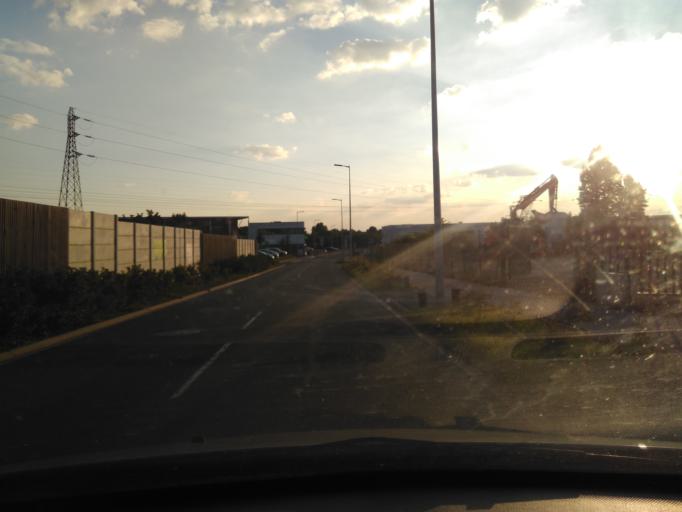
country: FR
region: Poitou-Charentes
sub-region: Departement de la Charente-Maritime
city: Puilboreau
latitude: 46.1762
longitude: -1.1182
